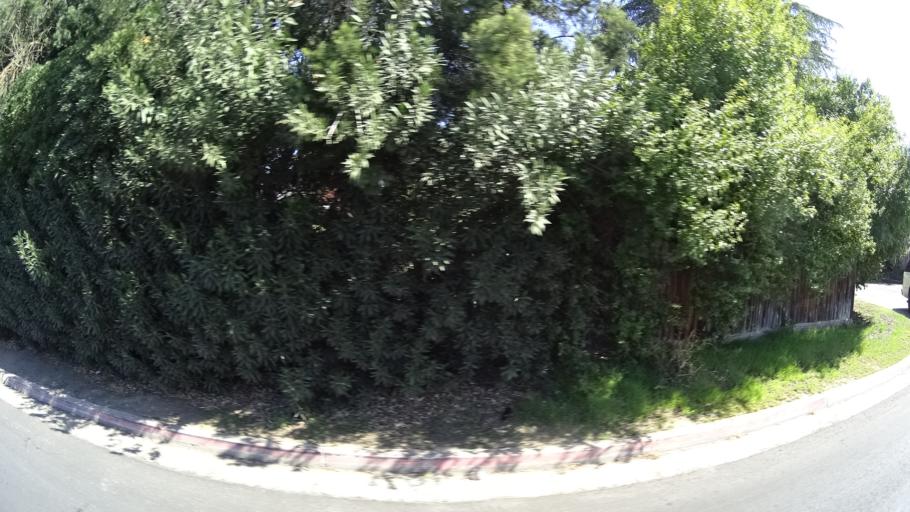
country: US
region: California
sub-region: Fresno County
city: Fresno
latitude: 36.7894
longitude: -119.8086
